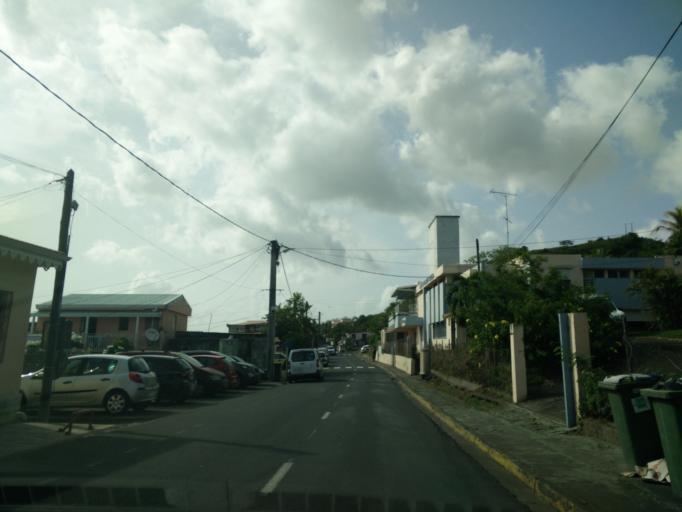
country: MQ
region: Martinique
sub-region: Martinique
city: Saint-Pierre
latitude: 14.7957
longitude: -61.2207
